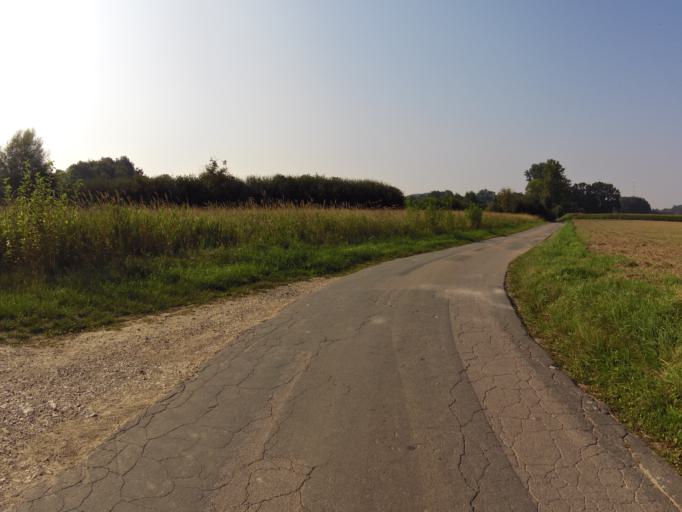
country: DE
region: North Rhine-Westphalia
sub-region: Regierungsbezirk Munster
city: Havixbeck
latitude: 51.9814
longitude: 7.3846
